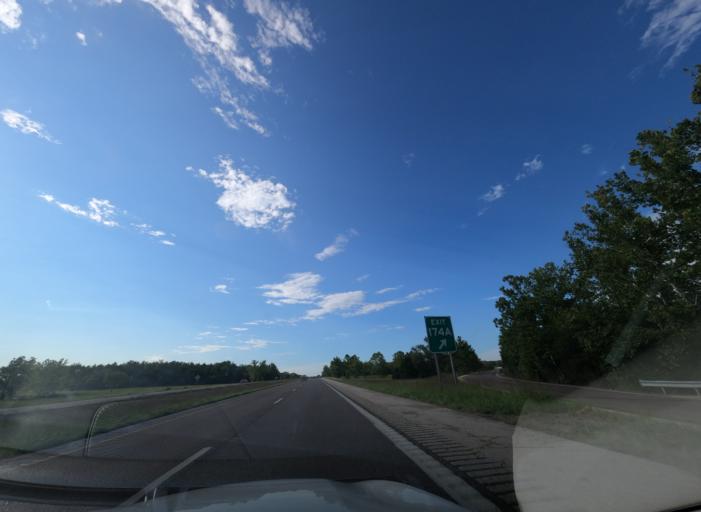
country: US
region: Missouri
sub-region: Jefferson County
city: Festus
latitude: 38.1942
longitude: -90.3972
